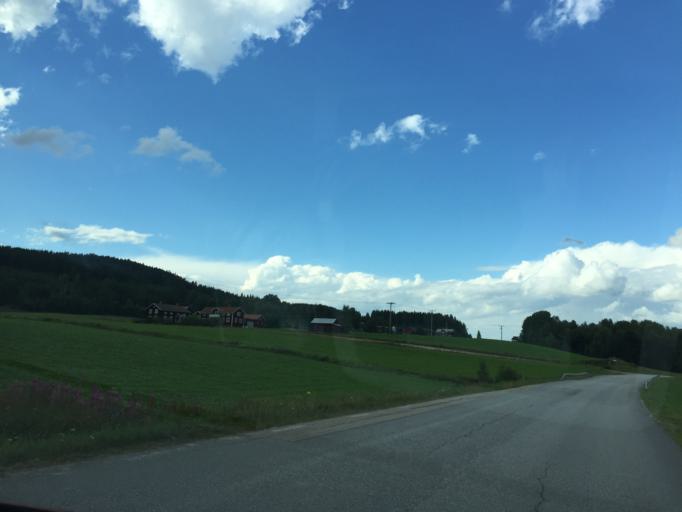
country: SE
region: Gaevleborg
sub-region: Ljusdals Kommun
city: Jaervsoe
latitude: 61.7045
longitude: 16.2995
